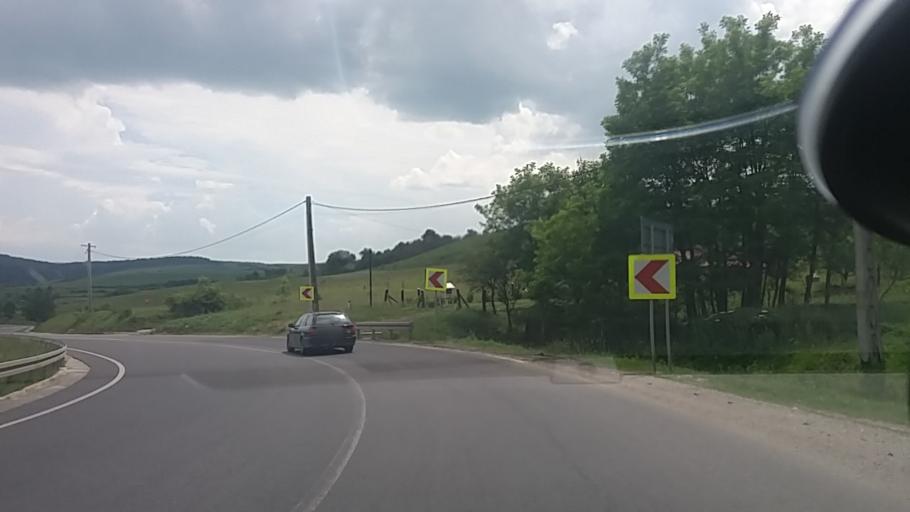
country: RO
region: Sibiu
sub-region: Comuna Slimnic
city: Slimnic
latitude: 45.9325
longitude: 24.1688
